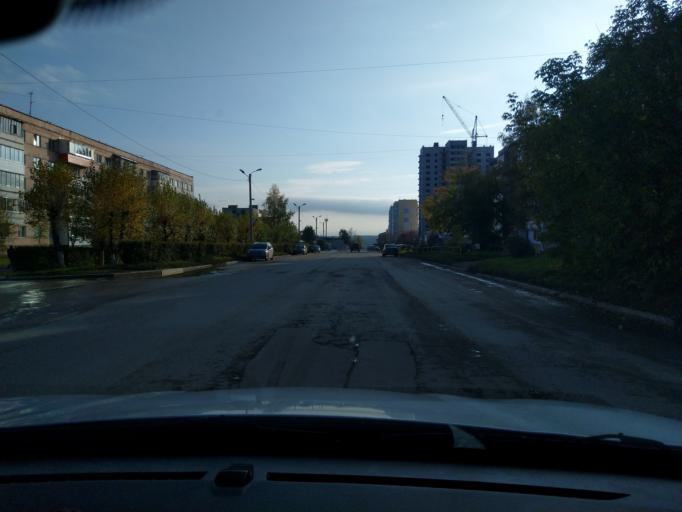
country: RU
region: Perm
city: Dobryanka
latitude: 58.4646
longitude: 56.4013
